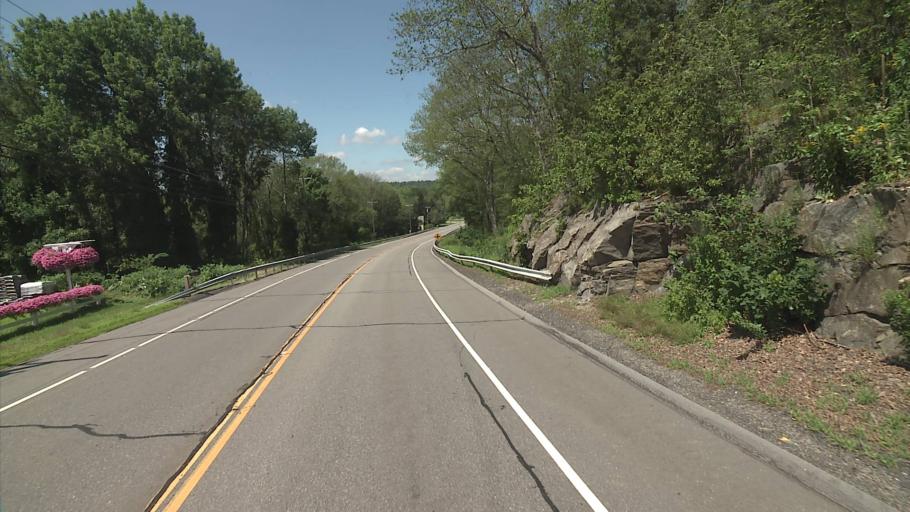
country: US
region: Connecticut
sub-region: Windham County
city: Plainfield Village
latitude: 41.6965
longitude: -71.9851
